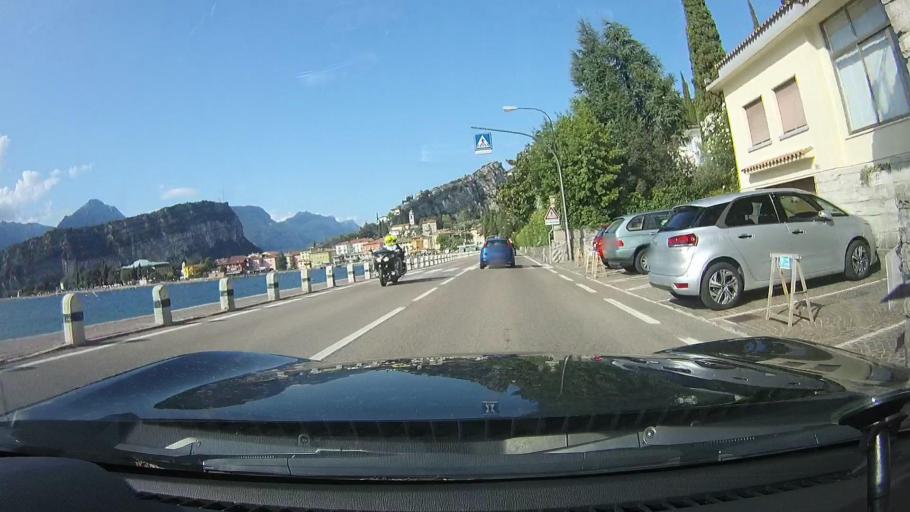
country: IT
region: Trentino-Alto Adige
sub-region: Provincia di Trento
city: Torbole sul Garda
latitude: 45.8654
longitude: 10.8757
